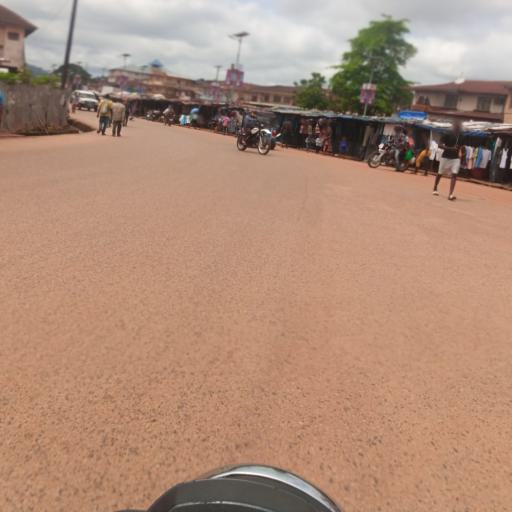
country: SL
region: Eastern Province
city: Kenema
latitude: 7.8767
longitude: -11.1898
